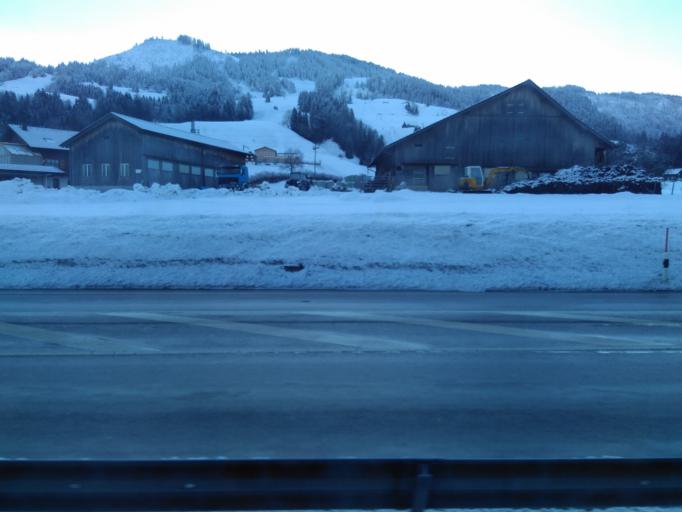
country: CH
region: Schwyz
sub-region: Bezirk Schwyz
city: Rothenthurm
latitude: 47.0944
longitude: 8.6702
